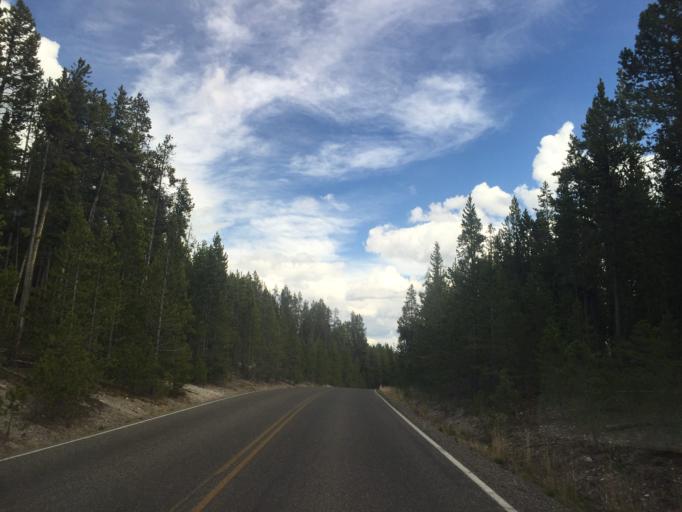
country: US
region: Montana
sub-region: Gallatin County
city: West Yellowstone
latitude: 44.7292
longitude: -110.4783
